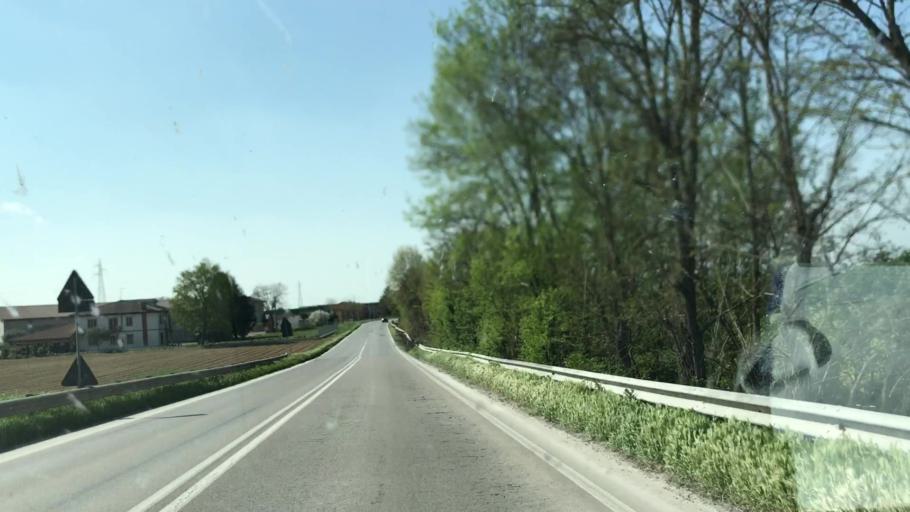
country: IT
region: Lombardy
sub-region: Provincia di Mantova
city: Soave
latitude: 45.2284
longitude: 10.7238
